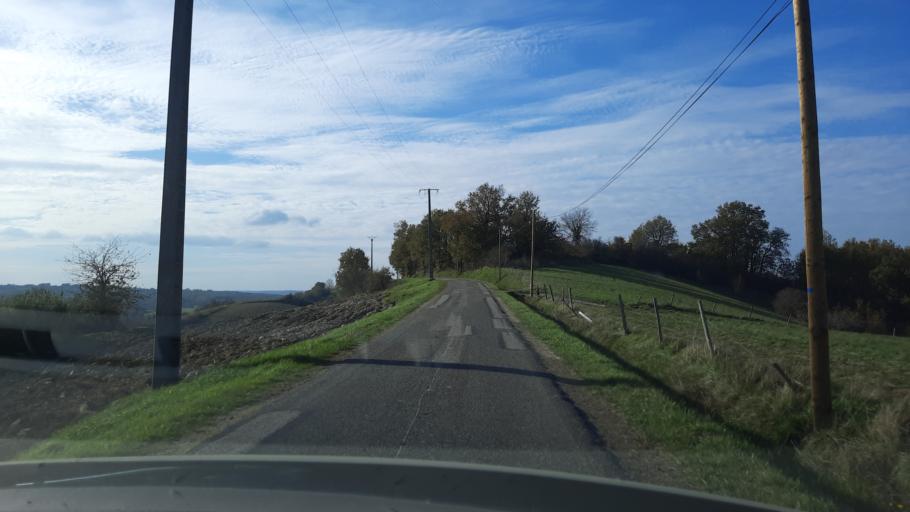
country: FR
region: Midi-Pyrenees
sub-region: Departement du Tarn-et-Garonne
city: Lafrancaise
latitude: 44.1517
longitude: 1.2866
